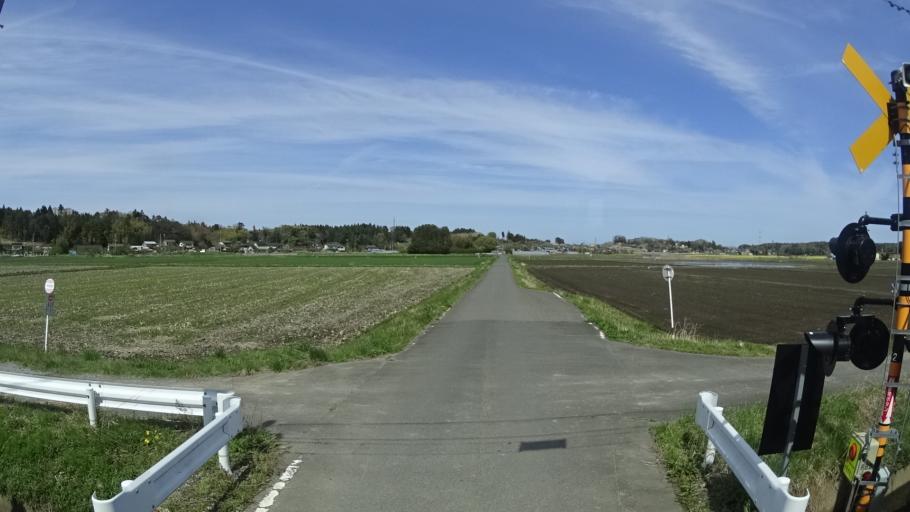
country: JP
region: Fukushima
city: Namie
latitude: 37.6065
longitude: 140.9899
